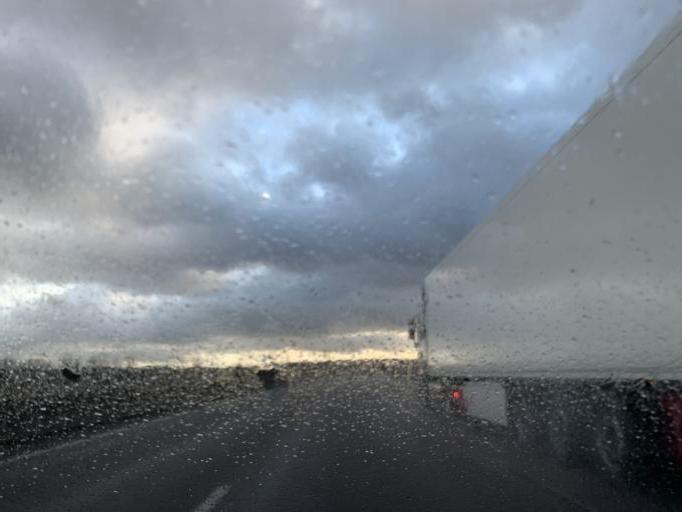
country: FR
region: Champagne-Ardenne
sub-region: Departement de la Haute-Marne
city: Langres
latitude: 47.8421
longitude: 5.2319
